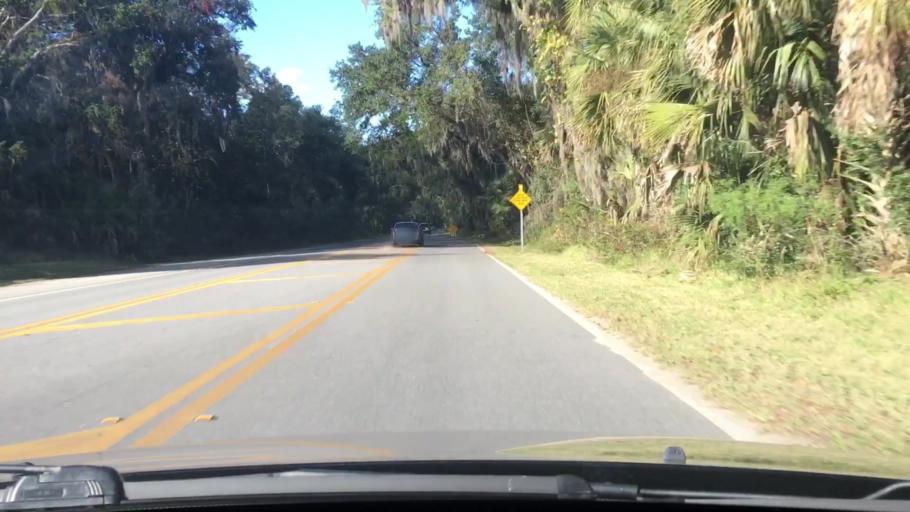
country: US
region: Florida
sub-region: Volusia County
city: Ormond-by-the-Sea
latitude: 29.3885
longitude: -81.1325
